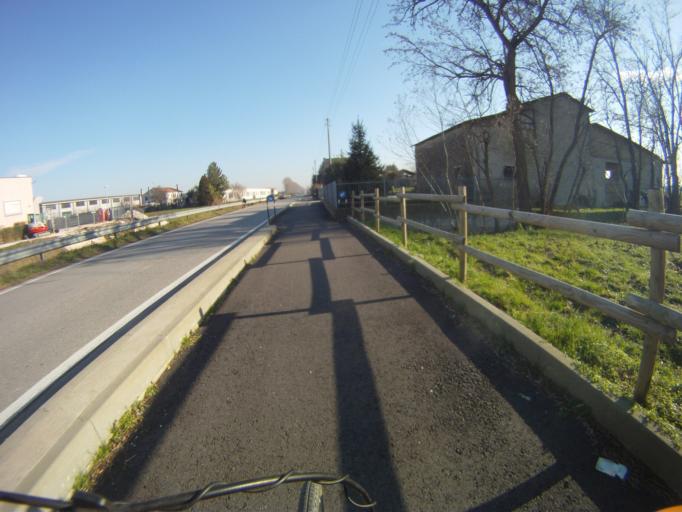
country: IT
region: Veneto
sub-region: Provincia di Padova
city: Brugine
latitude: 45.3077
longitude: 11.9940
